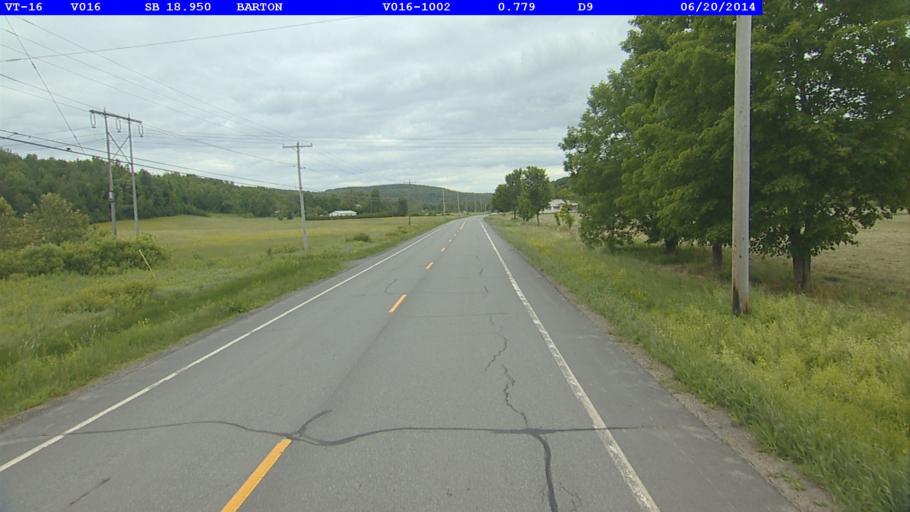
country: US
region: Vermont
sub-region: Orleans County
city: Newport
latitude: 44.7285
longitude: -72.1846
